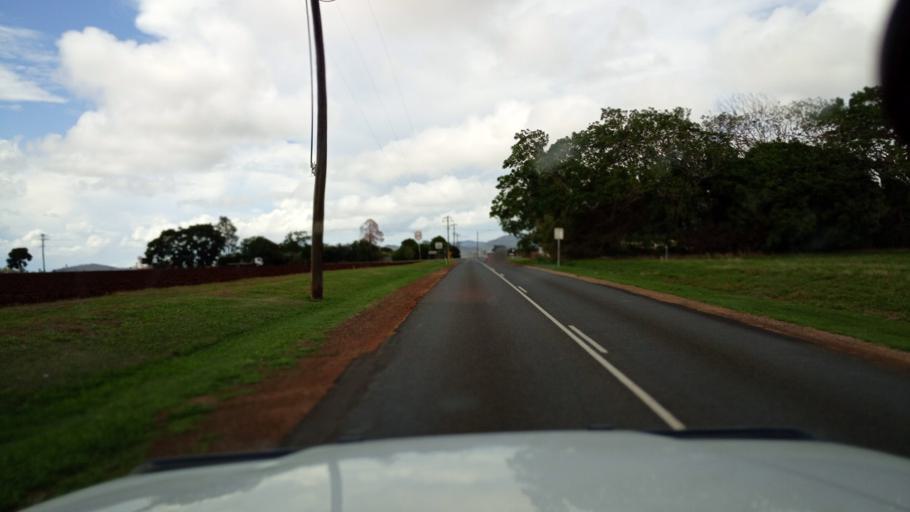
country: AU
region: Queensland
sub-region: Tablelands
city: Tolga
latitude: -17.2179
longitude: 145.5380
